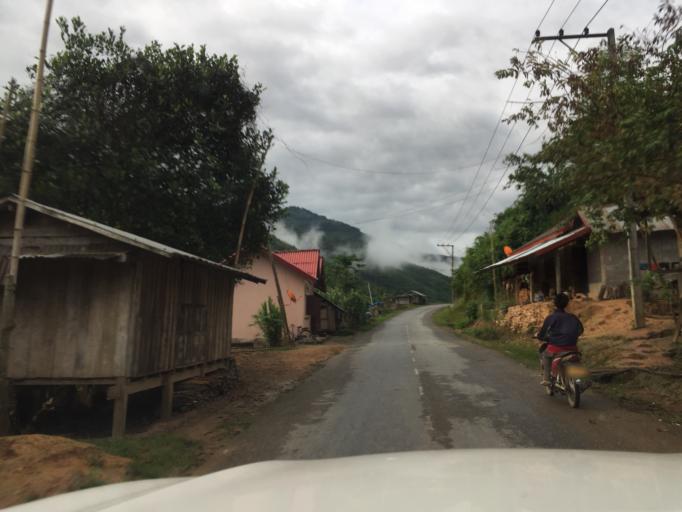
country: LA
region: Oudomxai
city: Muang La
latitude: 21.0525
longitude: 102.2411
